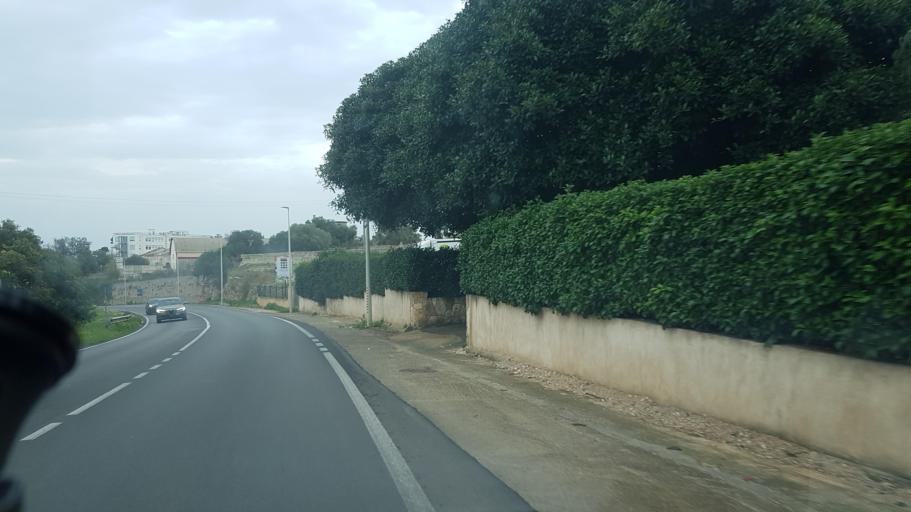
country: IT
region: Apulia
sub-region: Provincia di Brindisi
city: Ostuni
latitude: 40.7345
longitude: 17.5720
